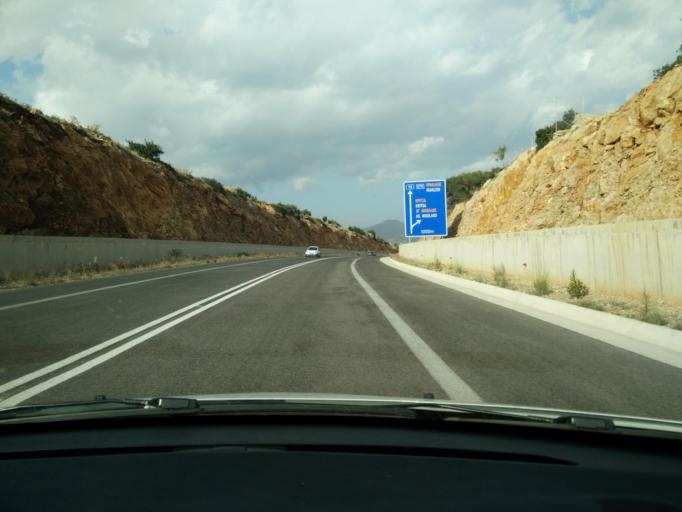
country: GR
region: Crete
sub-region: Nomos Lasithiou
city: Agios Nikolaos
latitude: 35.1725
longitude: 25.7011
